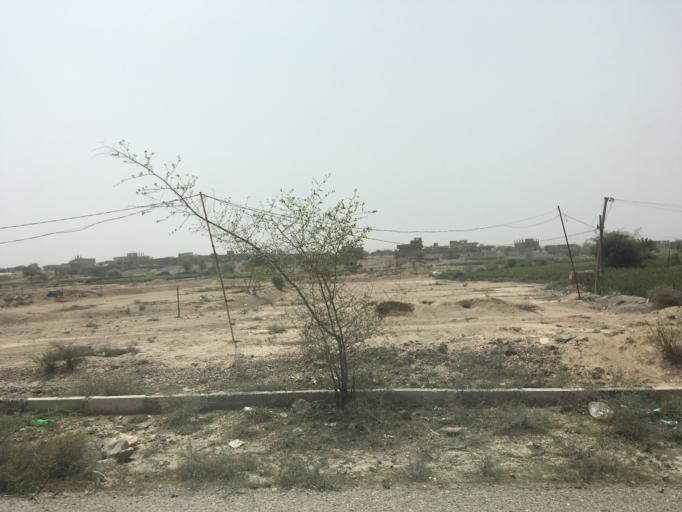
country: YE
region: Ad Dali'
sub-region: Qa'atabah
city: Qa`tabah
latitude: 13.8291
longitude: 44.7254
